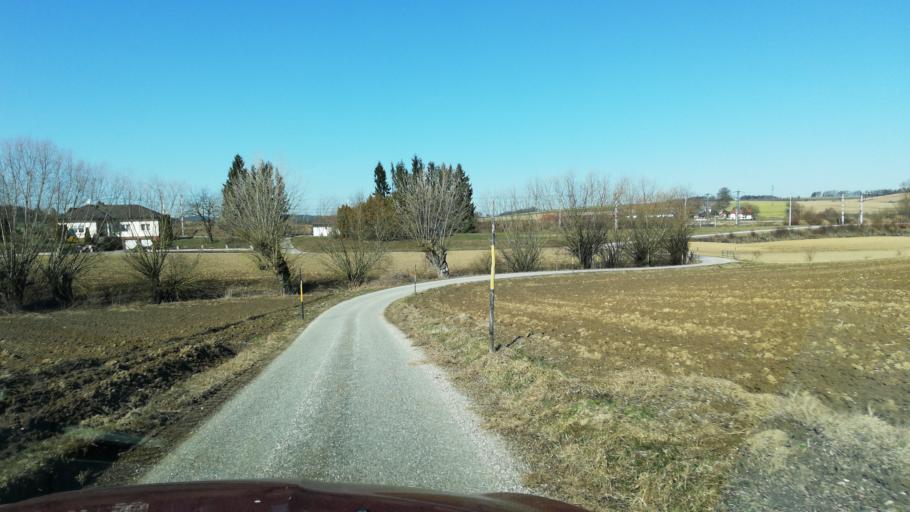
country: AT
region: Upper Austria
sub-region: Politischer Bezirk Vocklabruck
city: Schlatt
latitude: 48.0802
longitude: 13.8064
